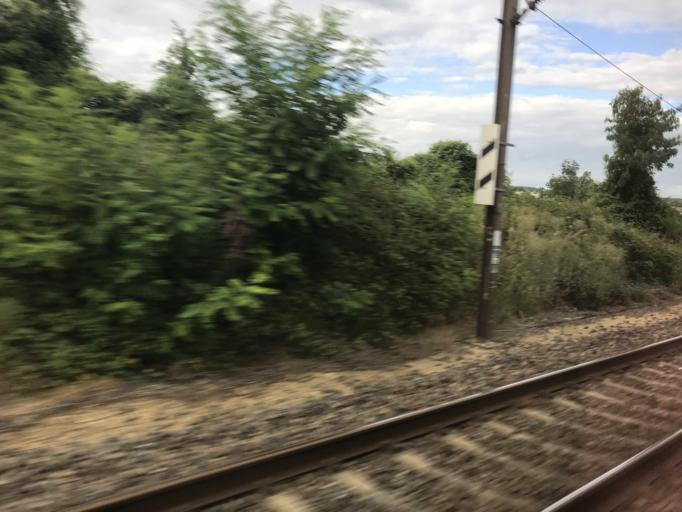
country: FR
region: Lorraine
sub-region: Departement de la Meuse
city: Stenay
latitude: 49.5236
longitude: 5.2712
